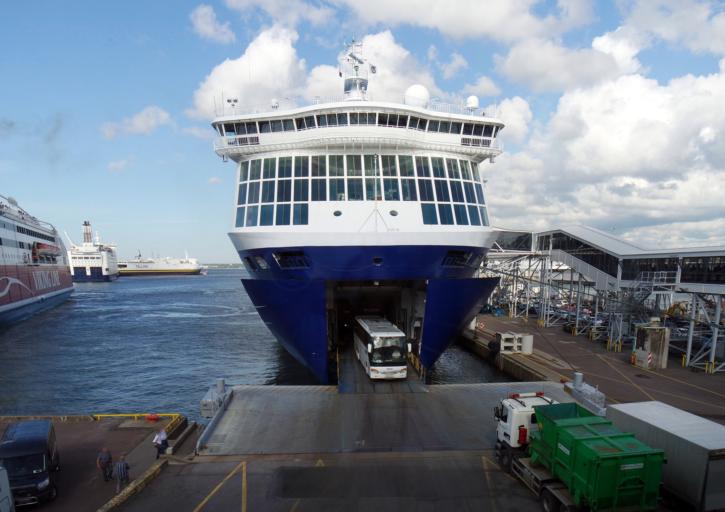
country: EE
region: Harju
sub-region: Tallinna linn
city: Tallinn
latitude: 59.4448
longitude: 24.7631
